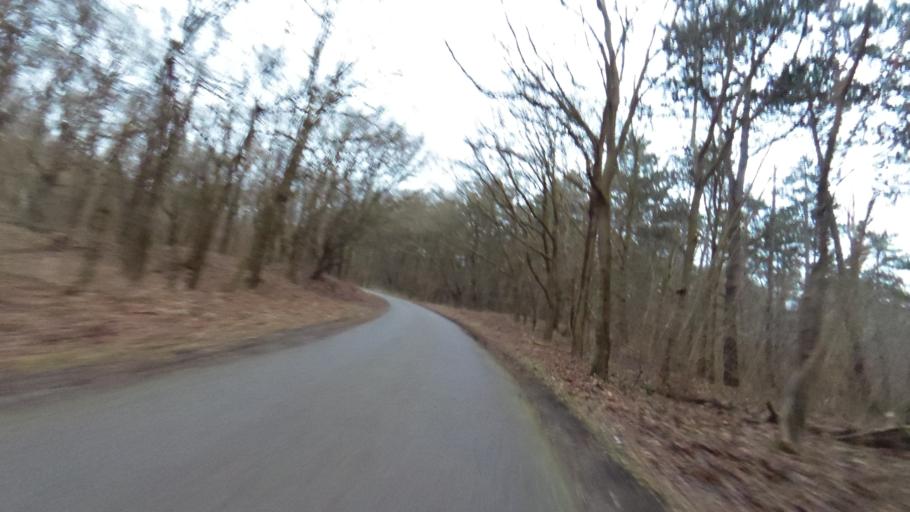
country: NL
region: North Holland
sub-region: Gemeente Castricum
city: Castricum
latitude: 52.5462
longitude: 4.6319
